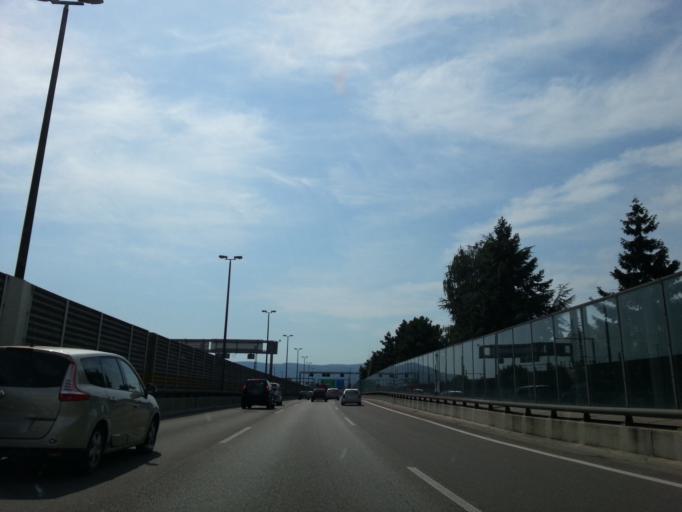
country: CH
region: Basel-Landschaft
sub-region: Bezirk Arlesheim
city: Birsfelden
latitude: 47.5616
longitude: 7.6114
